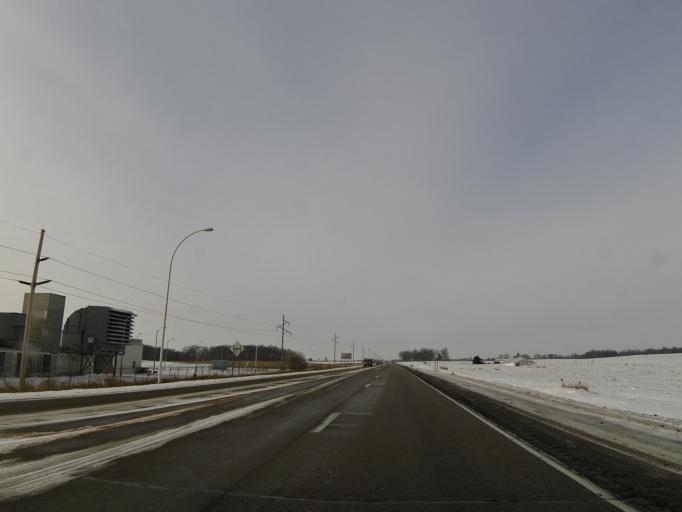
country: US
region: Minnesota
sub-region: Carver County
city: Waconia
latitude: 44.9055
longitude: -93.8200
